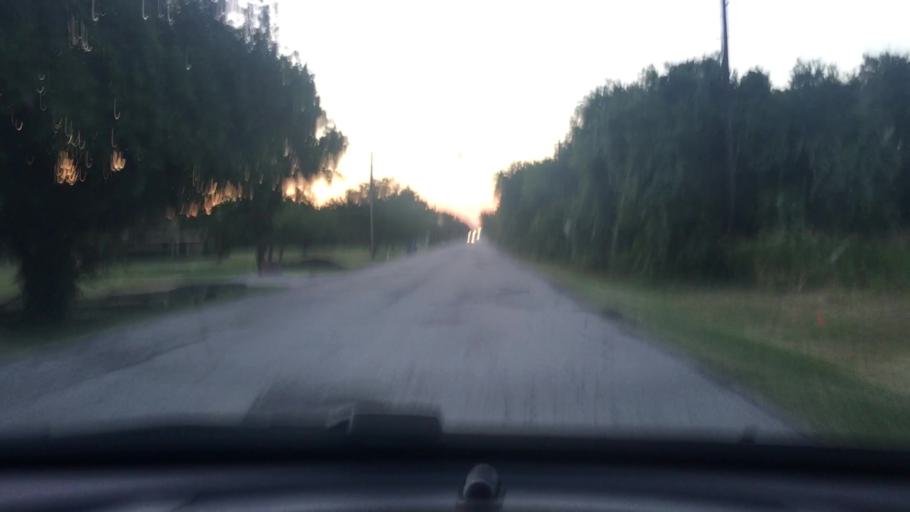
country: US
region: Texas
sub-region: Ellis County
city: Red Oak
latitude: 32.5607
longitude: -96.8110
